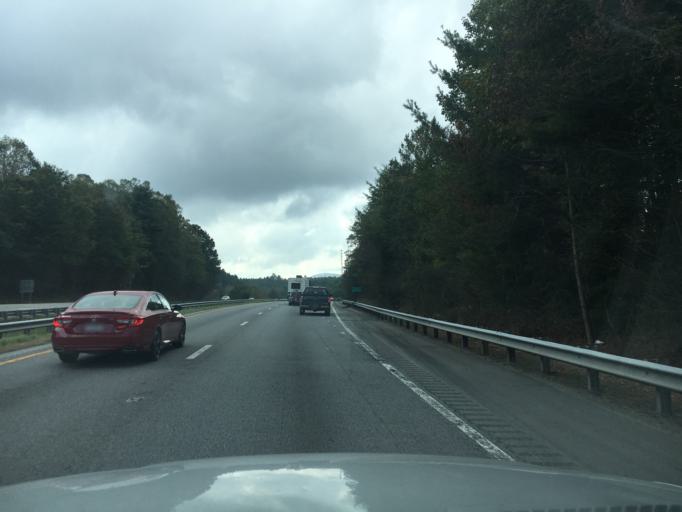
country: US
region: North Carolina
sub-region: Henderson County
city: East Flat Rock
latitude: 35.2898
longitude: -82.4019
